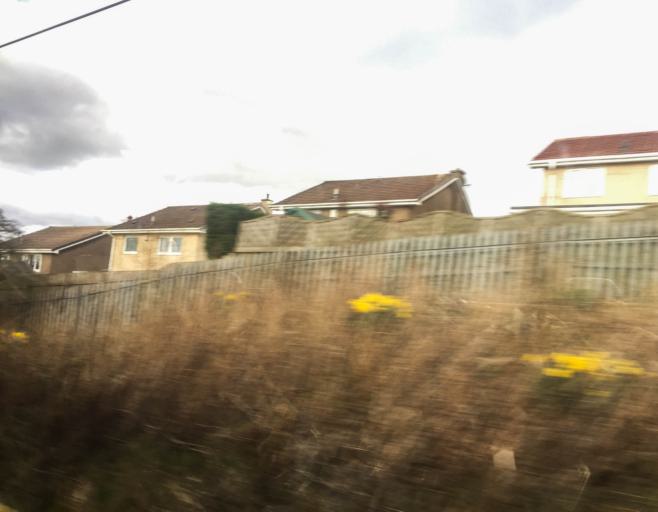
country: GB
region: Scotland
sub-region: South Lanarkshire
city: Carluke
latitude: 55.7264
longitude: -3.8427
